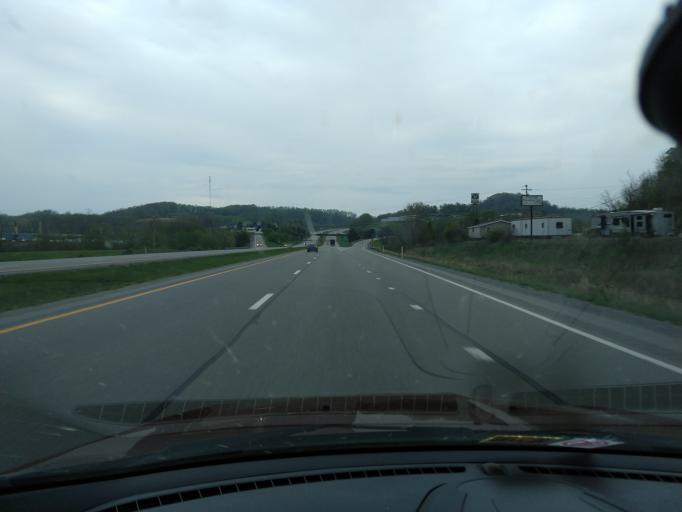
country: US
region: West Virginia
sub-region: Lewis County
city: Weston
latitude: 39.0996
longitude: -80.3920
